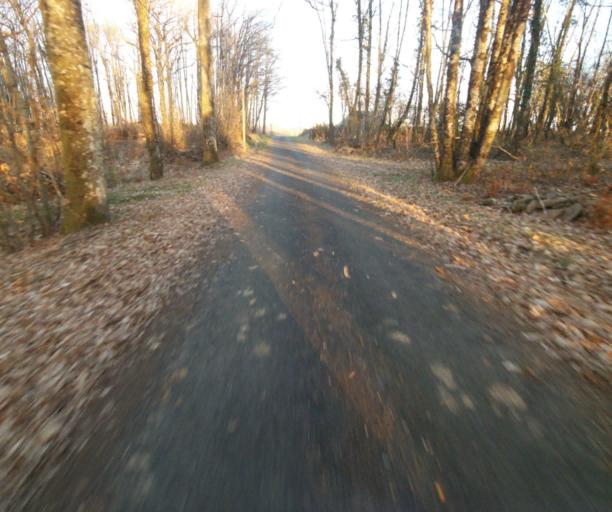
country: FR
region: Limousin
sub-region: Departement de la Correze
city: Uzerche
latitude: 45.3663
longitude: 1.6053
